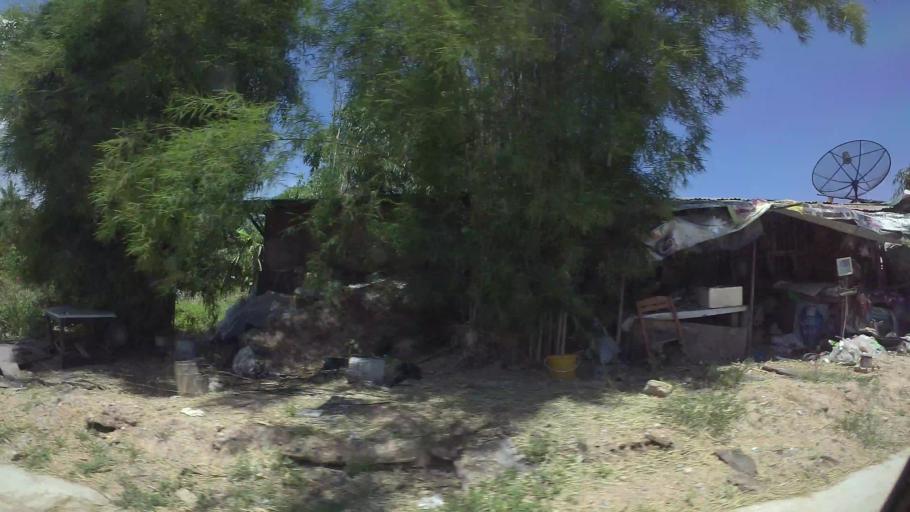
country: TH
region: Chon Buri
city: Si Racha
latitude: 13.1331
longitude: 100.9427
